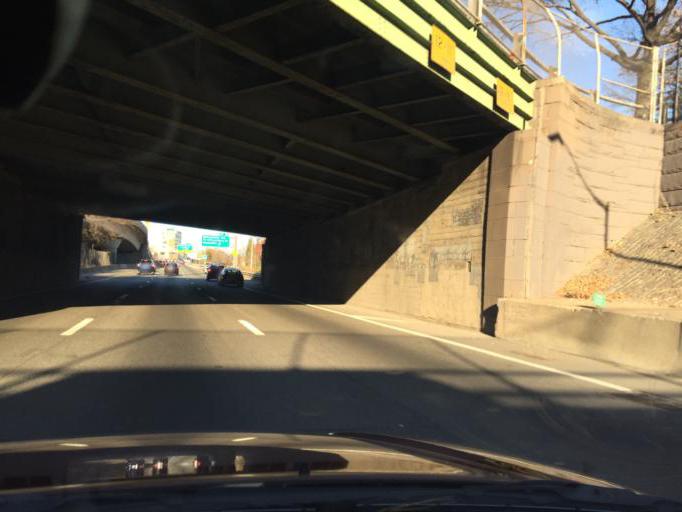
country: US
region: New York
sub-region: Queens County
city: Long Island City
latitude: 40.7102
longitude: -73.9559
